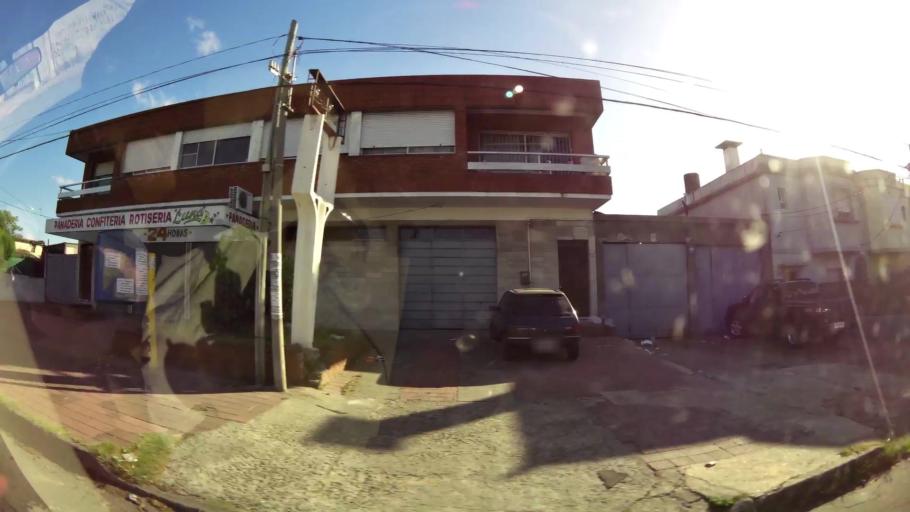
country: UY
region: Montevideo
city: Montevideo
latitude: -34.8543
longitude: -56.2354
